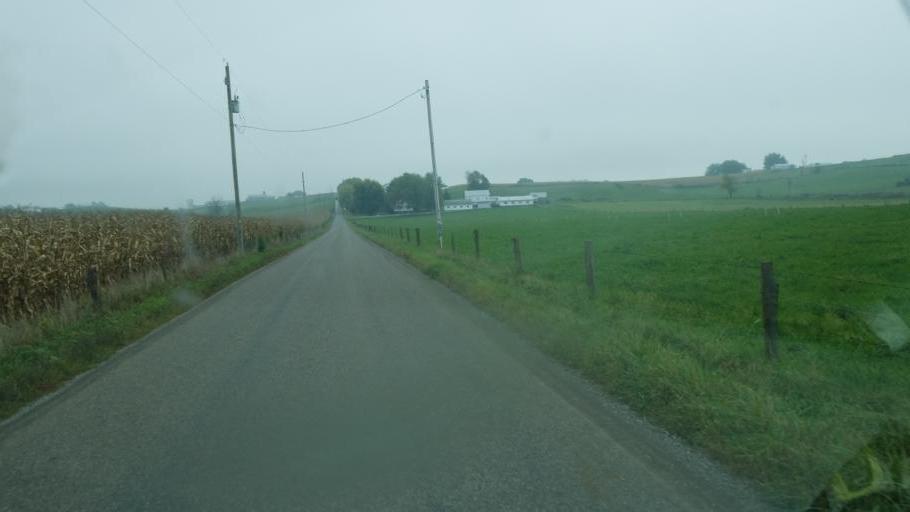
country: US
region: Ohio
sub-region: Holmes County
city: Millersburg
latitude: 40.5641
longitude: -81.7794
